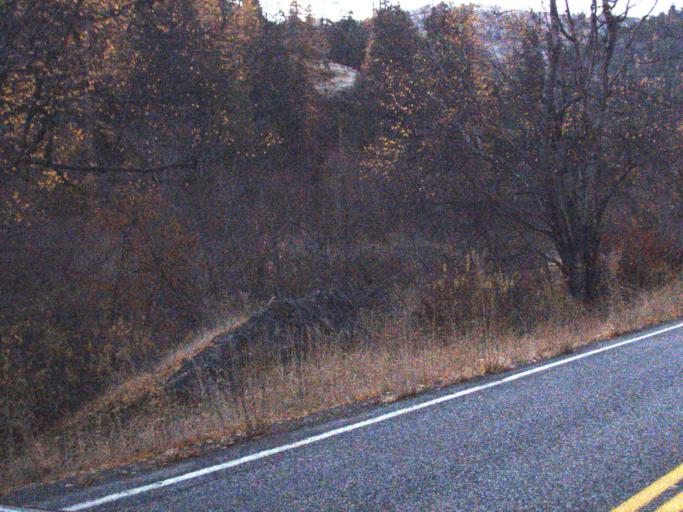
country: US
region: Washington
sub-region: Ferry County
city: Republic
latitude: 48.4854
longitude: -118.7388
